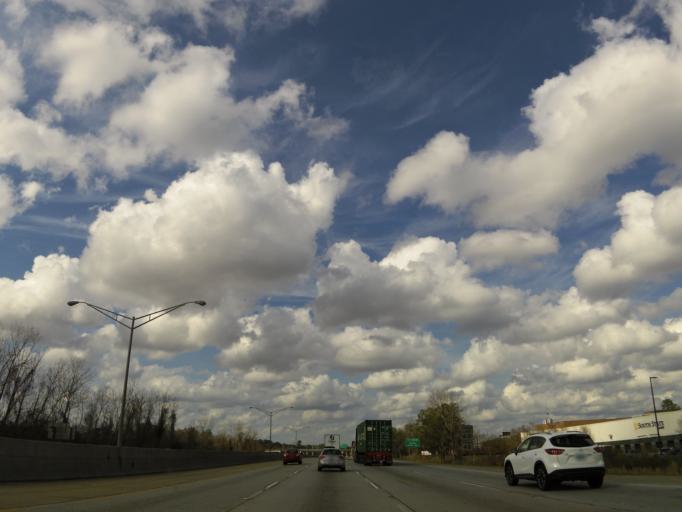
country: US
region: South Carolina
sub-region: Berkeley County
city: Hanahan
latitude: 32.8772
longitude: -80.0156
